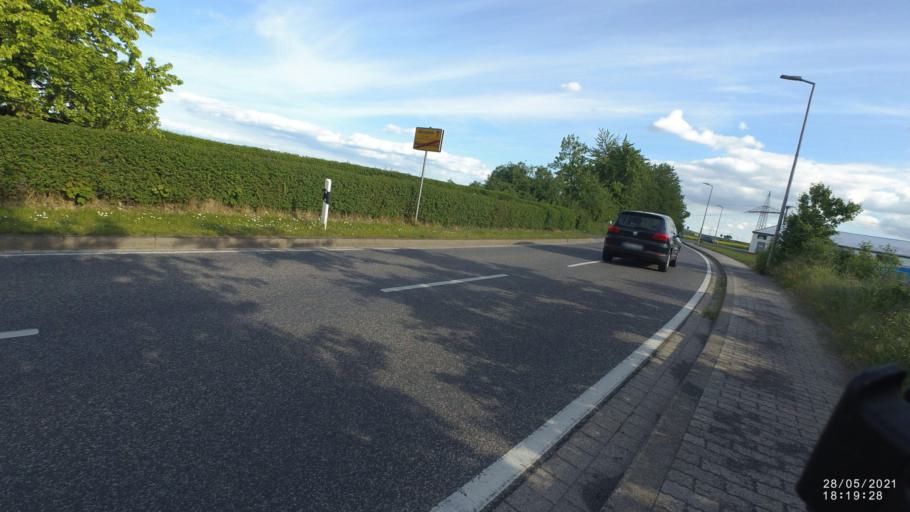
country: DE
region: Rheinland-Pfalz
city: Munstermaifeld
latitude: 50.2426
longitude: 7.3627
